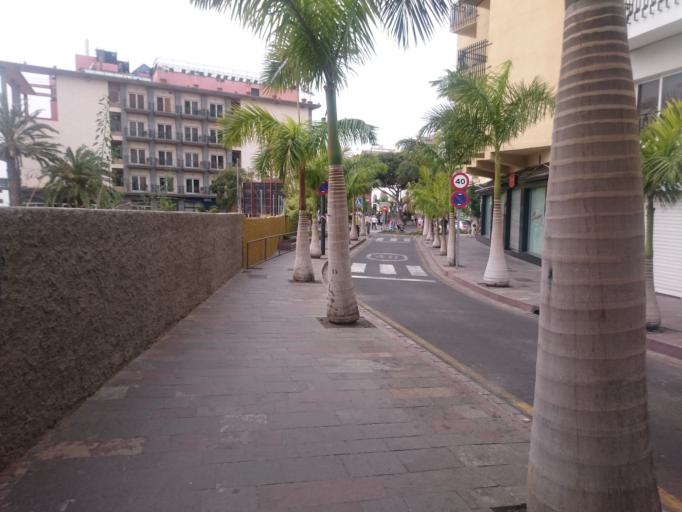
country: ES
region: Canary Islands
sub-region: Provincia de Santa Cruz de Tenerife
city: Playa de las Americas
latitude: 28.0522
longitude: -16.7162
